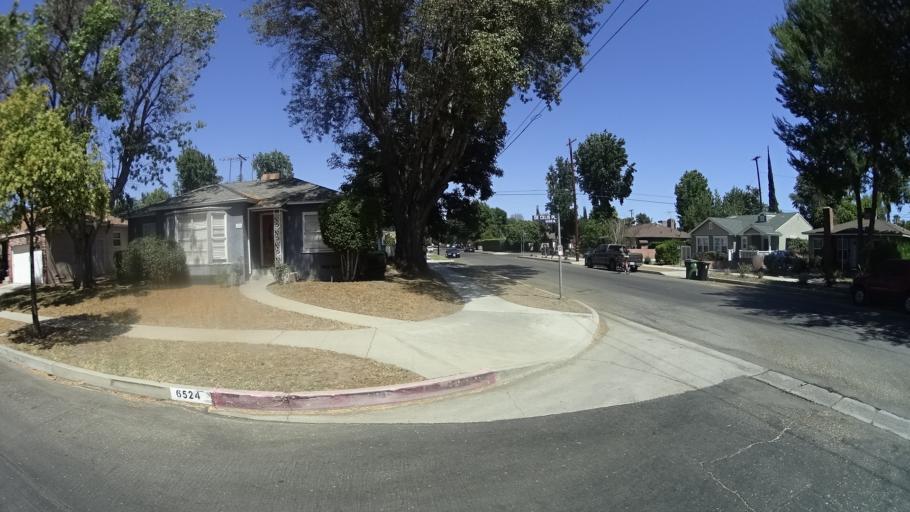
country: US
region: California
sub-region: Los Angeles County
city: Van Nuys
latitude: 34.1894
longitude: -118.4944
